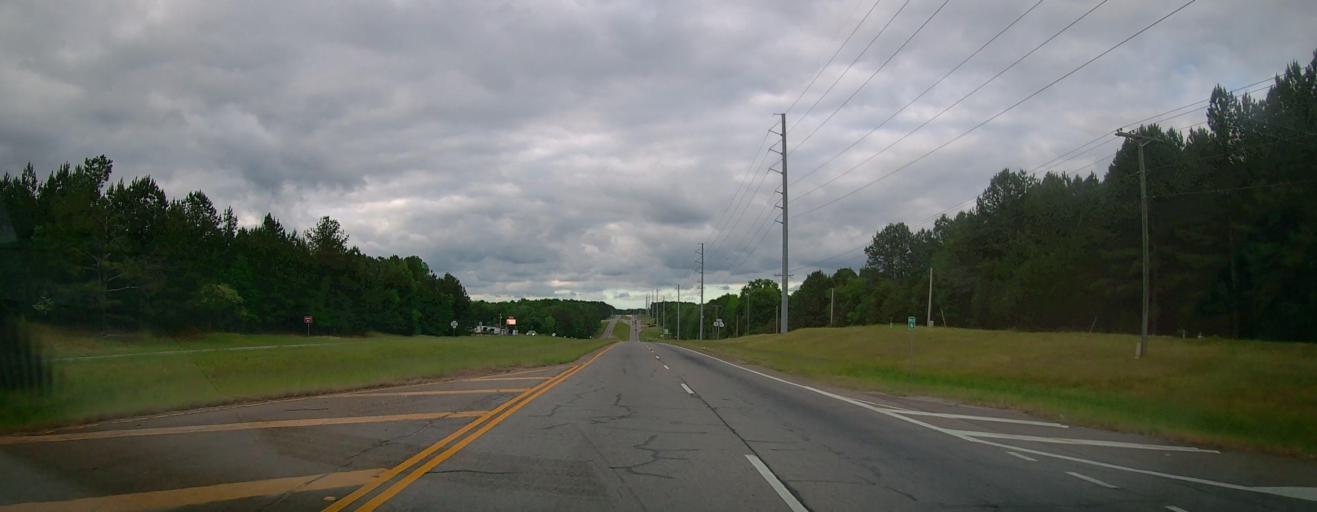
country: US
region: Georgia
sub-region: Oconee County
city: Bogart
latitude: 33.9258
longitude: -83.5116
